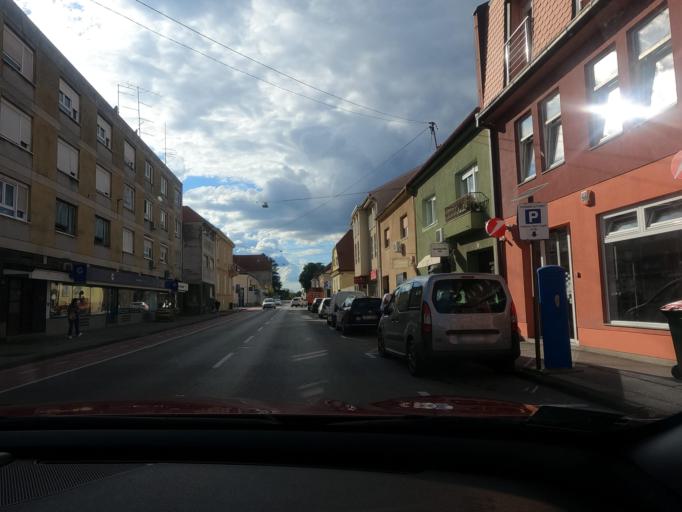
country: HR
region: Sisacko-Moslavacka
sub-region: Grad Sisak
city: Sisak
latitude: 45.4874
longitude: 16.3736
